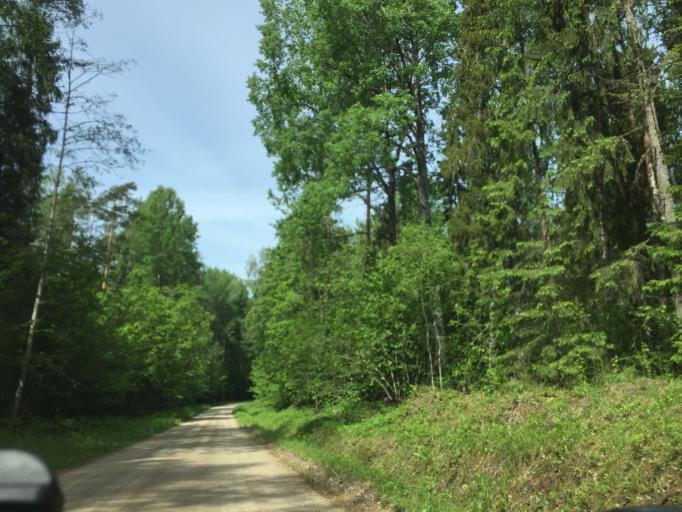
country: LV
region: Koceni
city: Koceni
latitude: 57.4528
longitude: 25.2729
